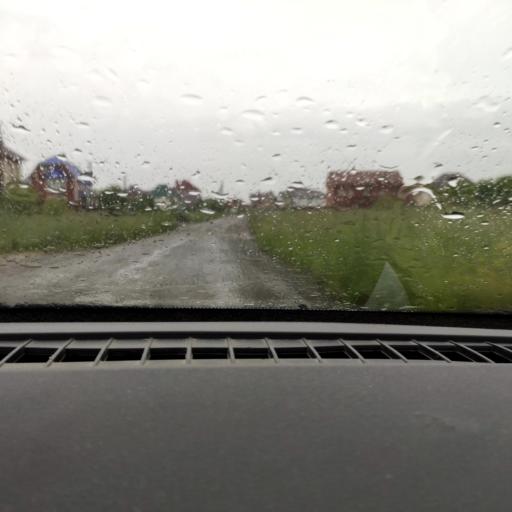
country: RU
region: Perm
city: Perm
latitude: 58.0424
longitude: 56.3734
